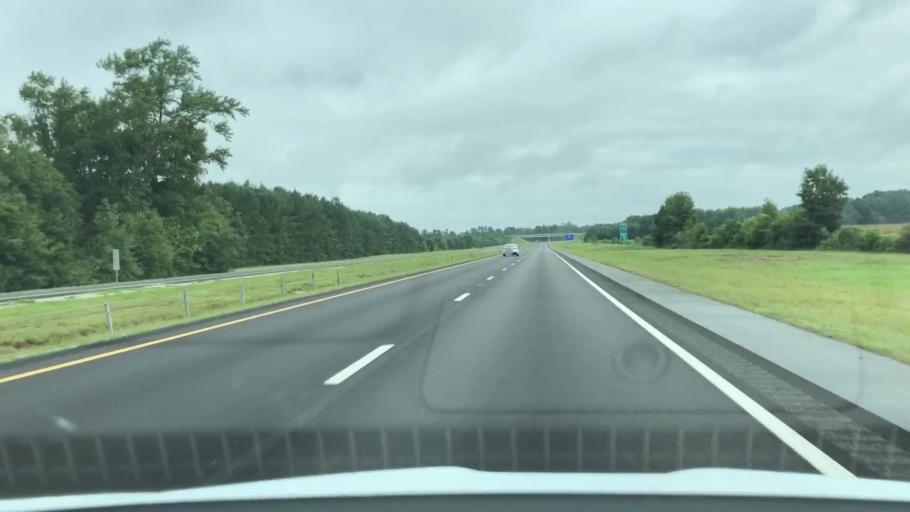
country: US
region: North Carolina
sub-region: Wayne County
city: Fremont
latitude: 35.5320
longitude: -77.9892
